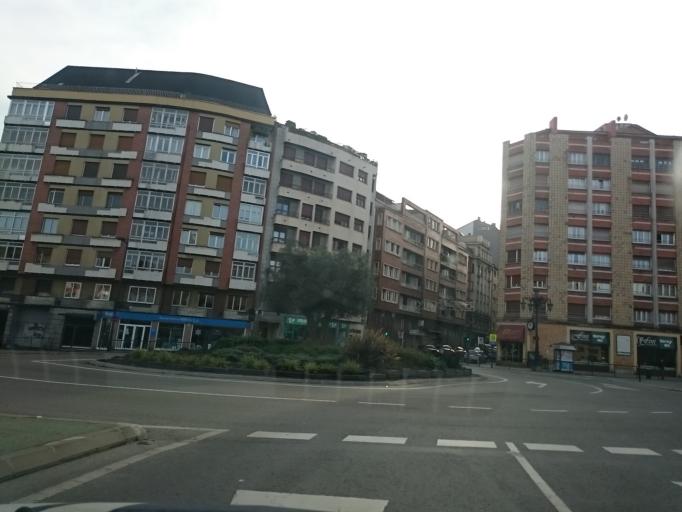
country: ES
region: Asturias
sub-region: Province of Asturias
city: Oviedo
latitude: 43.3664
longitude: -5.8448
